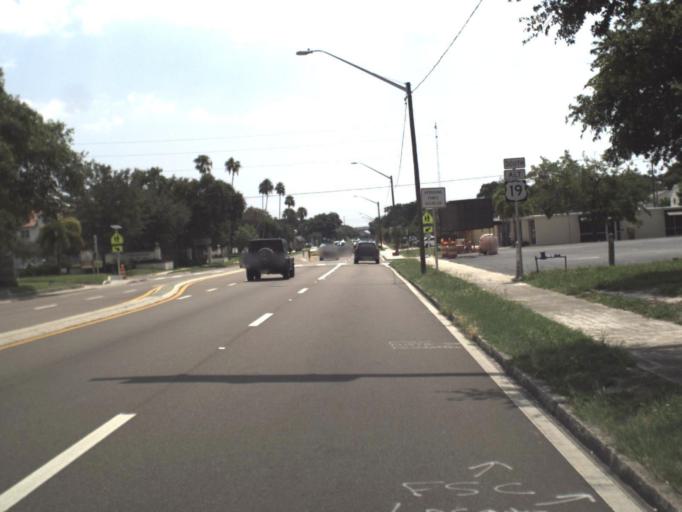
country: US
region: Florida
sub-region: Pinellas County
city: Saint Petersburg
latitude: 27.7773
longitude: -82.6709
